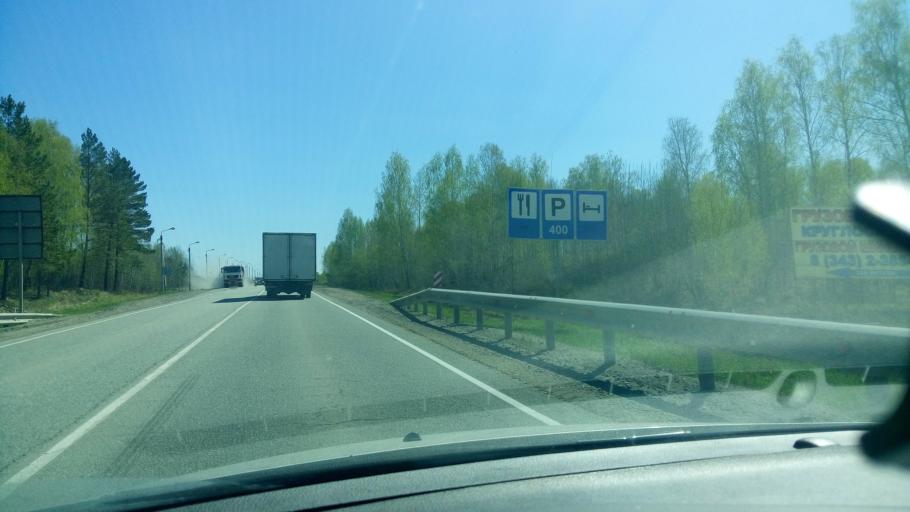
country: RU
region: Sverdlovsk
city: Yelanskiy
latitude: 56.7585
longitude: 62.3433
